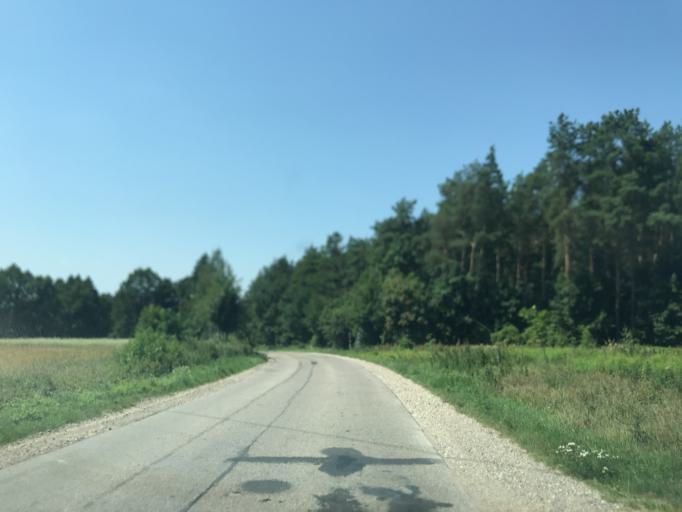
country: PL
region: Kujawsko-Pomorskie
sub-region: Powiat lipnowski
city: Chrostkowo
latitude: 52.9841
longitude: 19.3080
